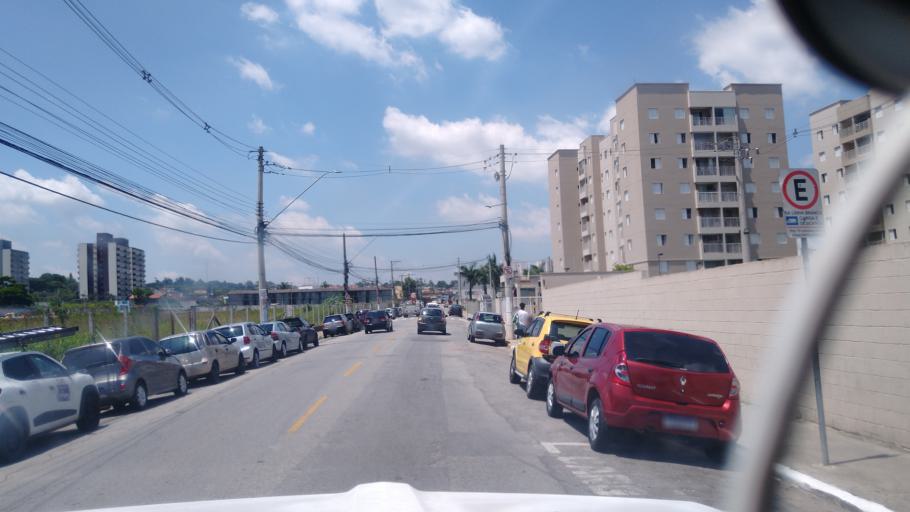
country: BR
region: Sao Paulo
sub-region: Suzano
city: Suzano
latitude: -23.5468
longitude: -46.3176
